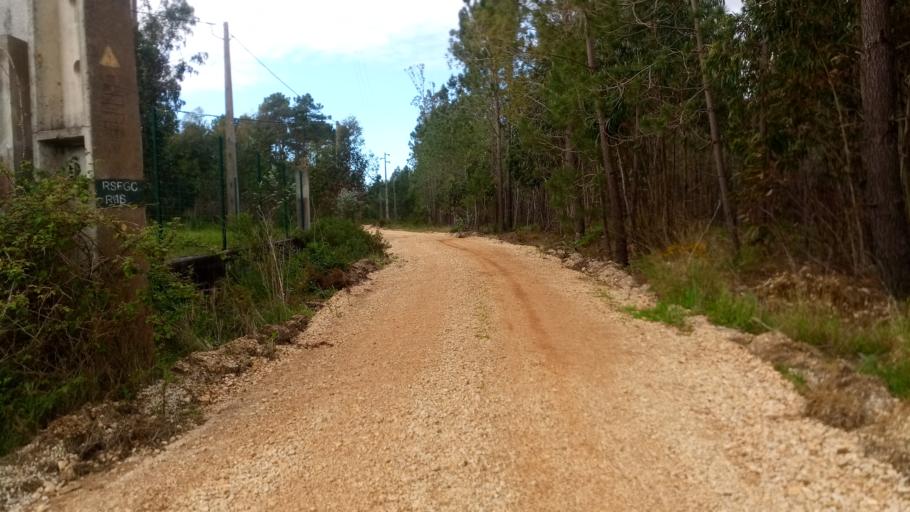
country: PT
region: Leiria
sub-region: Caldas da Rainha
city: Caldas da Rainha
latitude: 39.4445
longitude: -9.1652
